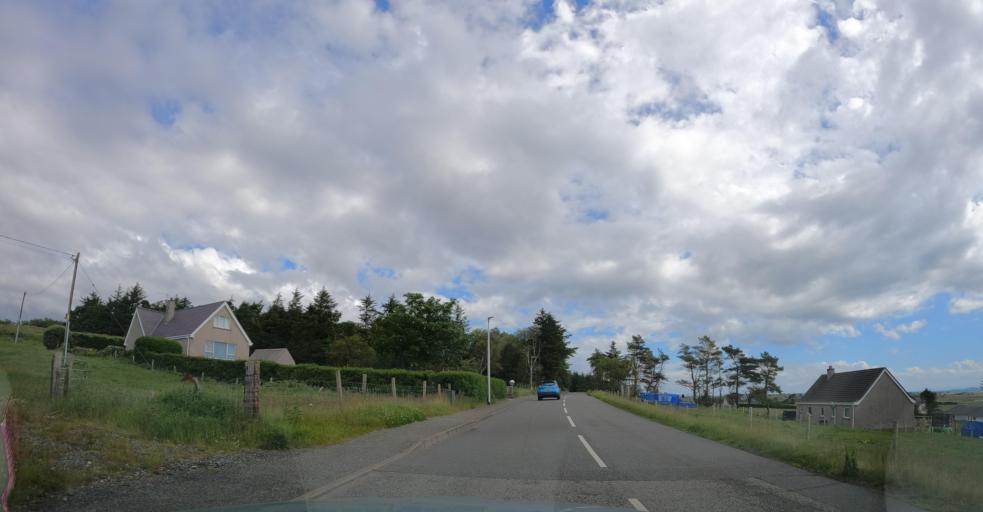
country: GB
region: Scotland
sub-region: Eilean Siar
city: Isle of Lewis
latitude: 58.2347
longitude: -6.3904
